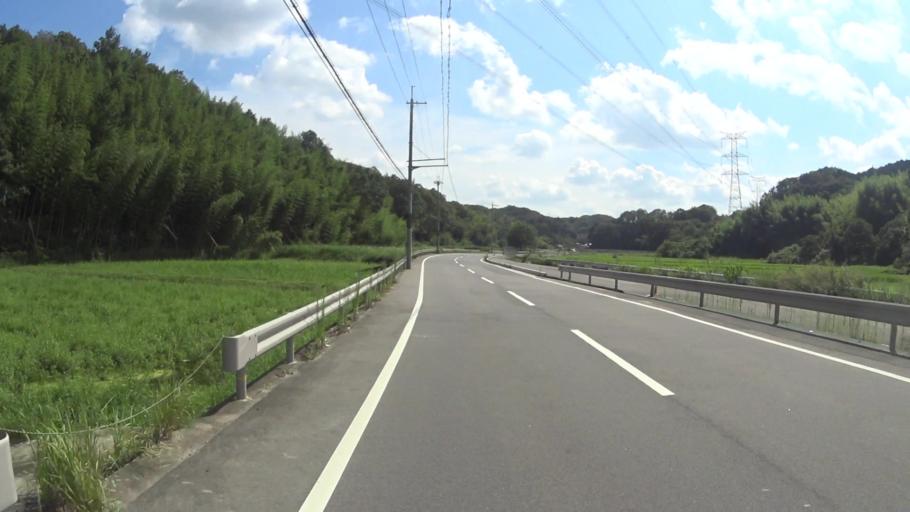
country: JP
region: Kyoto
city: Tanabe
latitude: 34.7788
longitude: 135.7540
